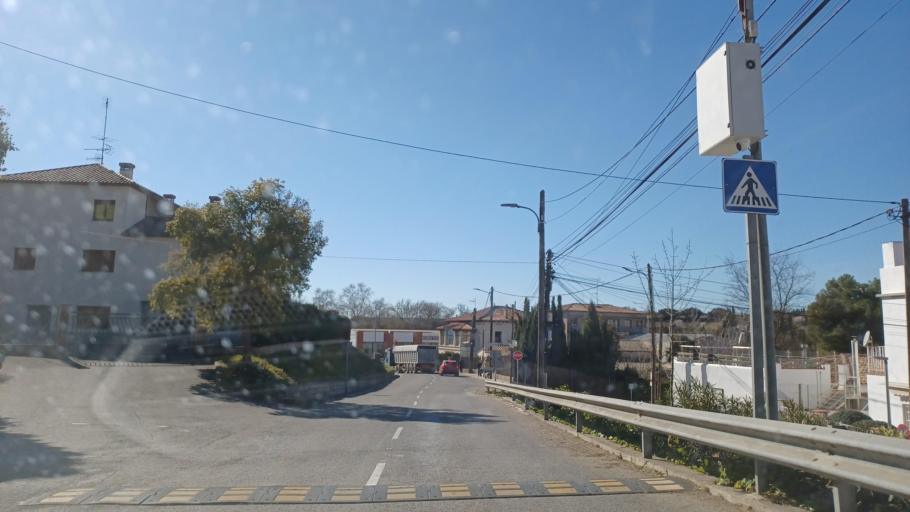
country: ES
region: Catalonia
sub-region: Provincia de Barcelona
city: Vilafranca del Penedes
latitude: 41.3551
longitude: 1.6698
